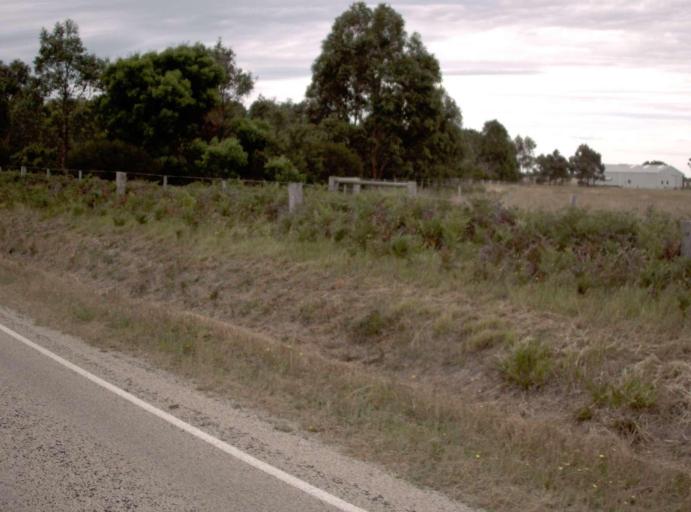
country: AU
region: Victoria
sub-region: East Gippsland
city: Bairnsdale
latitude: -37.9118
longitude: 147.5506
